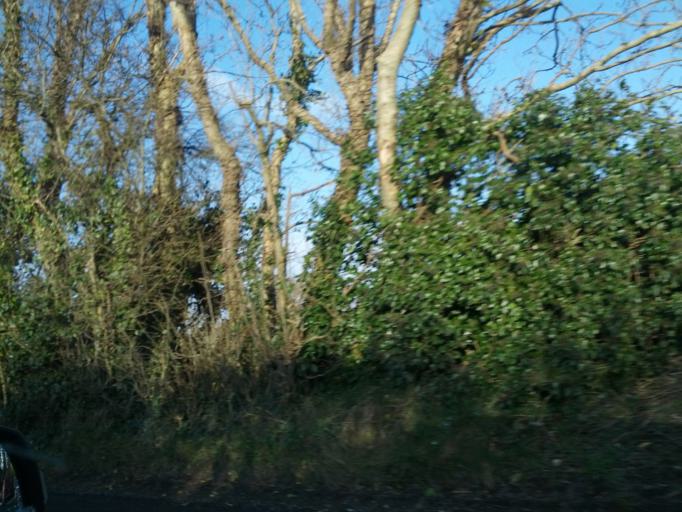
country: IE
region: Connaught
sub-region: County Galway
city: Gort
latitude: 53.1614
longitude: -8.7819
